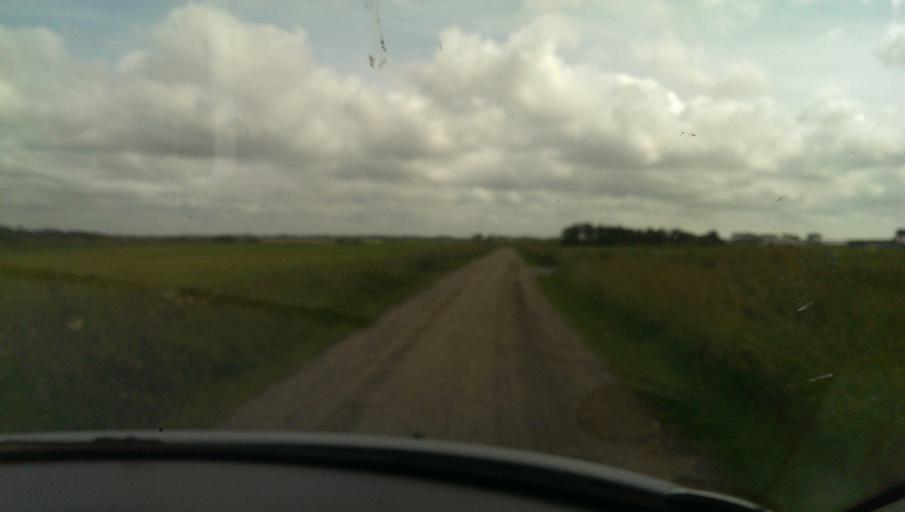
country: DK
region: Central Jutland
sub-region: Holstebro Kommune
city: Ulfborg
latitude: 56.2942
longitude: 8.2809
